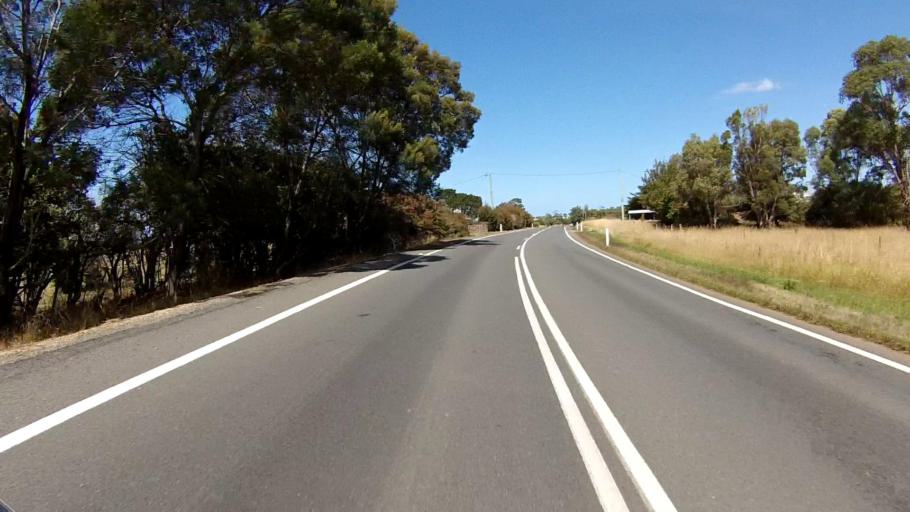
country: AU
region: Tasmania
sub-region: Break O'Day
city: St Helens
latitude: -42.0699
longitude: 148.0656
